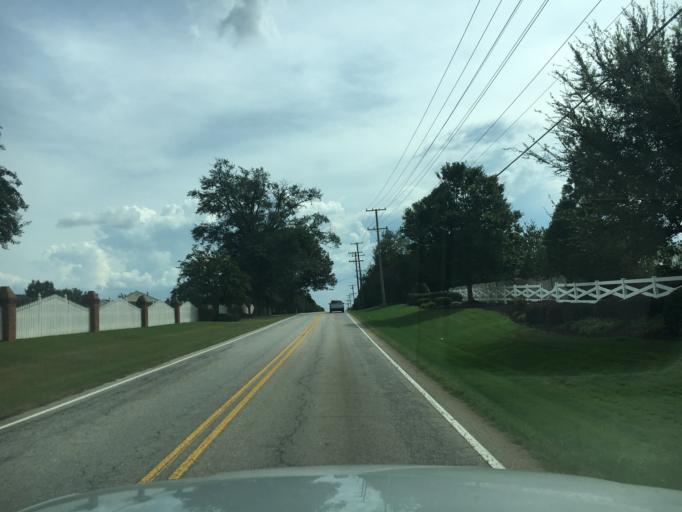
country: US
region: South Carolina
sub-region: Greenville County
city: Greer
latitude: 34.8864
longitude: -82.2416
